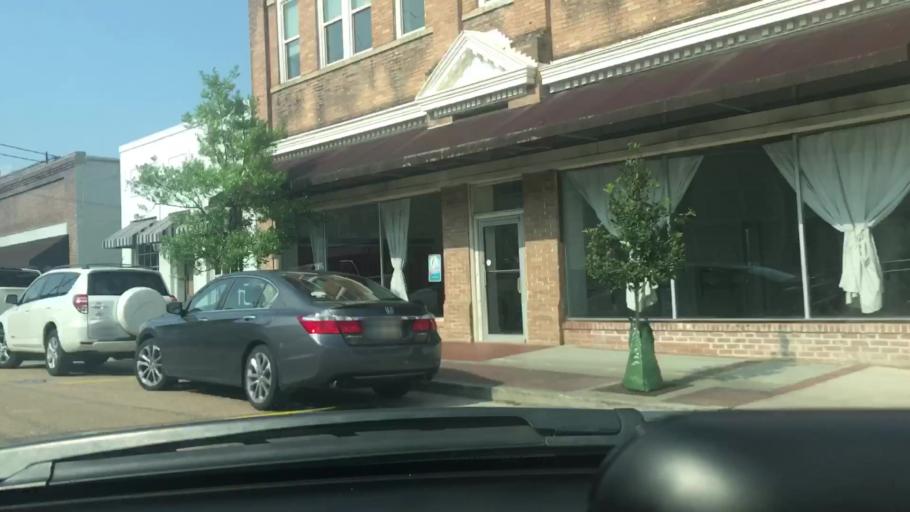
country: US
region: Louisiana
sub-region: Tangipahoa Parish
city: Hammond
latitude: 30.5035
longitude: -90.4594
